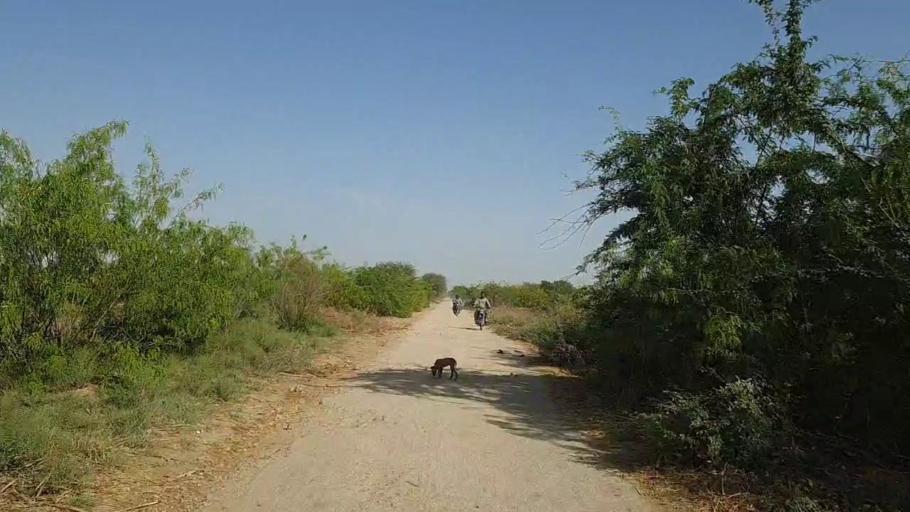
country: PK
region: Sindh
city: Kotri
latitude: 25.1675
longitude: 68.2866
